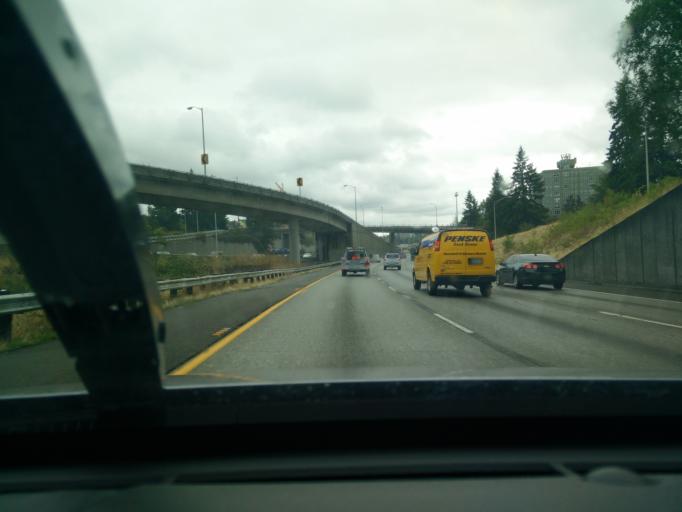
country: US
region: Washington
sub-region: King County
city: Seattle
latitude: 47.6817
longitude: -122.3214
